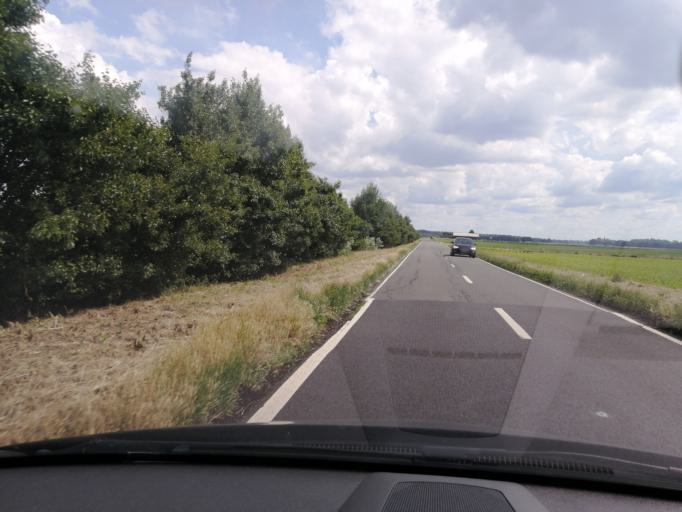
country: GB
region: England
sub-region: Cambridgeshire
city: Yaxley
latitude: 52.5023
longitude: -0.2523
